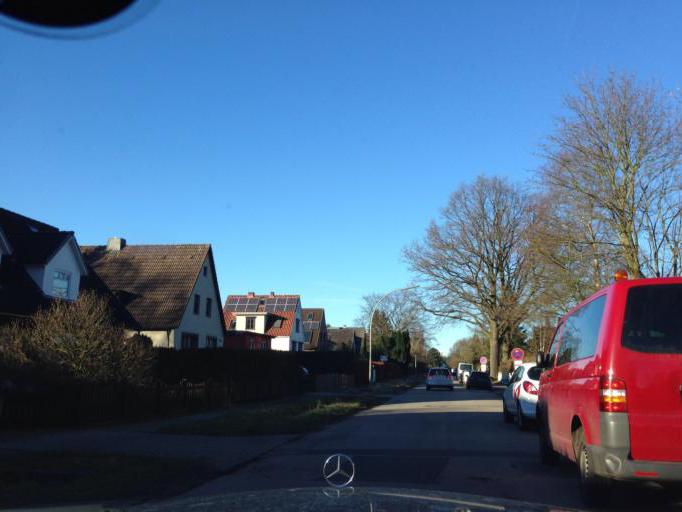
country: DE
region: Hamburg
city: Farmsen-Berne
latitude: 53.6073
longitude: 10.1287
